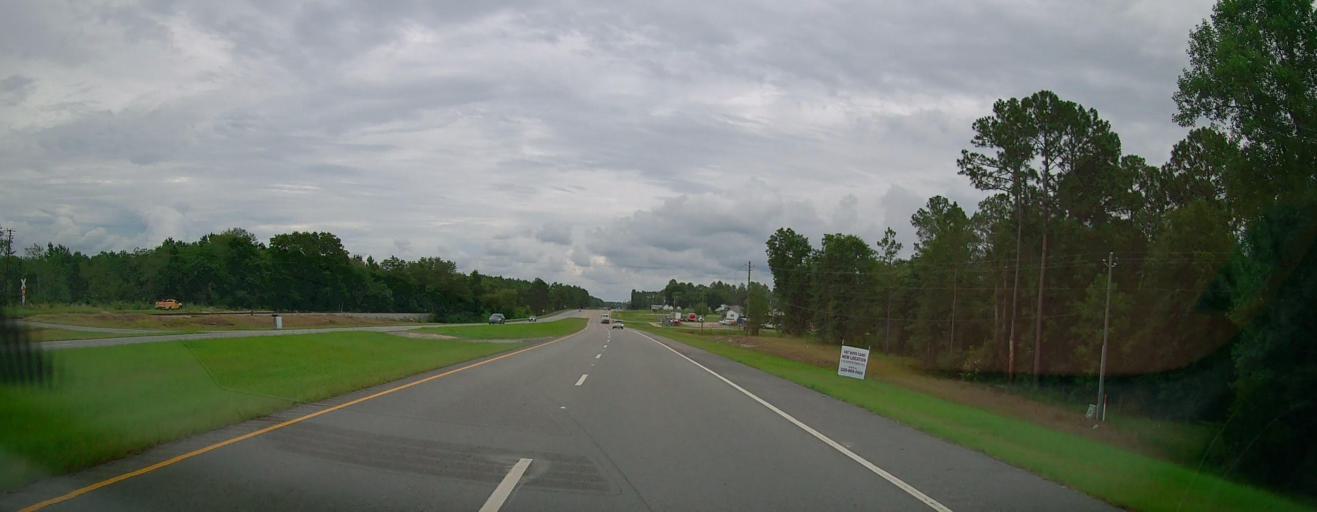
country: US
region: Georgia
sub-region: Telfair County
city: Helena
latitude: 32.0847
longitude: -82.9307
